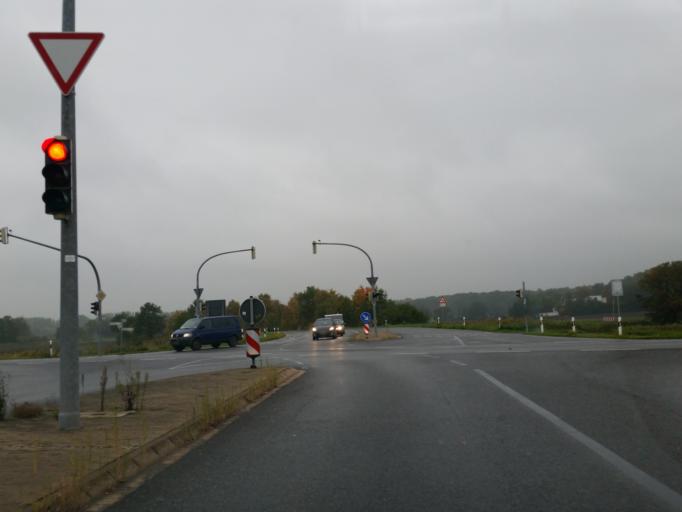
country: DE
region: Lower Saxony
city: Cremlingen
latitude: 52.2503
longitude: 10.5966
